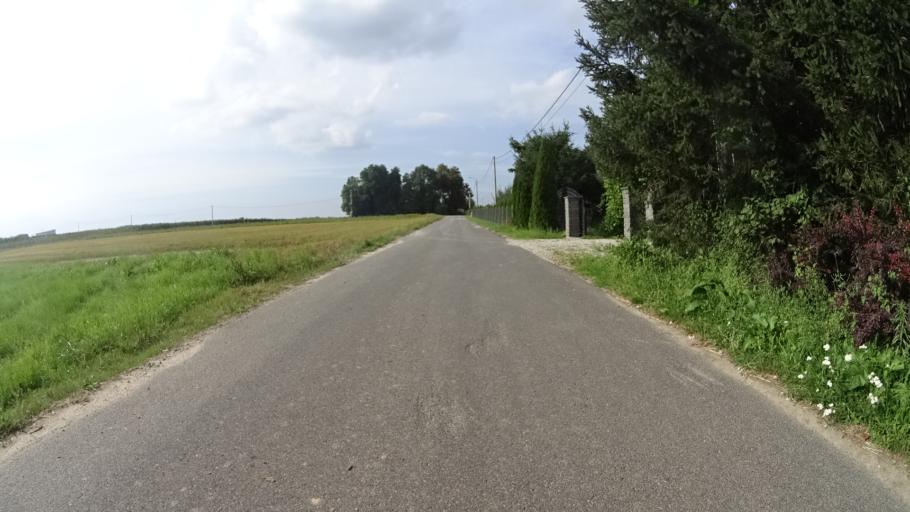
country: PL
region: Masovian Voivodeship
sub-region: Powiat grojecki
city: Goszczyn
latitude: 51.7086
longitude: 20.8417
